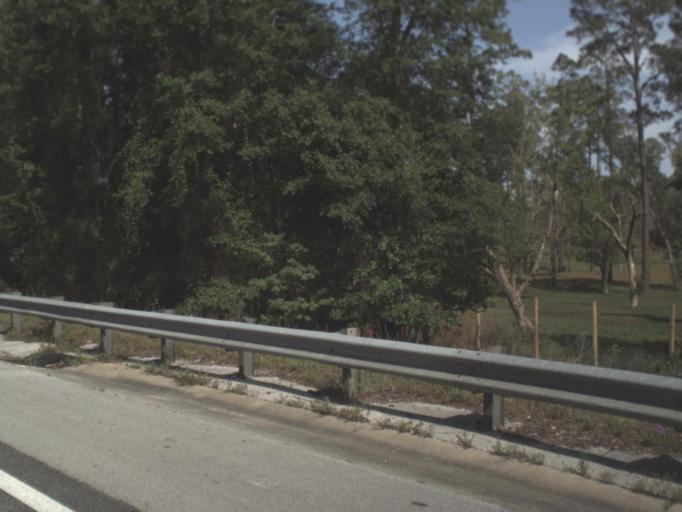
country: US
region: Florida
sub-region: Santa Rosa County
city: Bagdad
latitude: 30.5882
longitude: -87.0075
